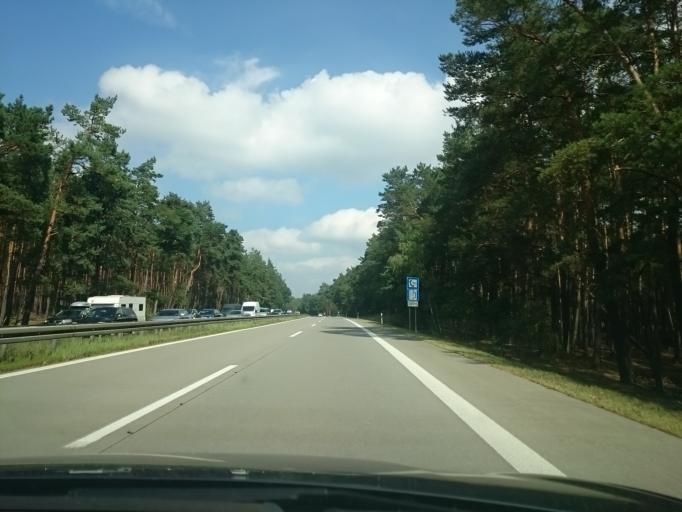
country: DE
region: Brandenburg
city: Marienwerder
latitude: 52.8312
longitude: 13.6582
